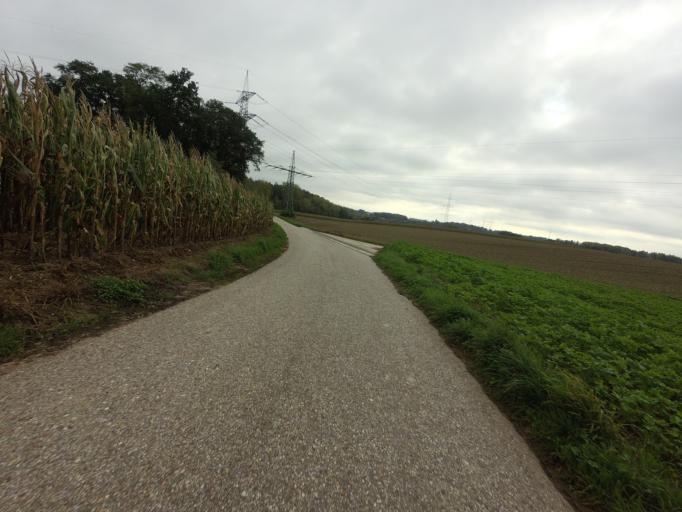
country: DE
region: North Rhine-Westphalia
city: Geilenkirchen
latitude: 50.9792
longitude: 6.1315
